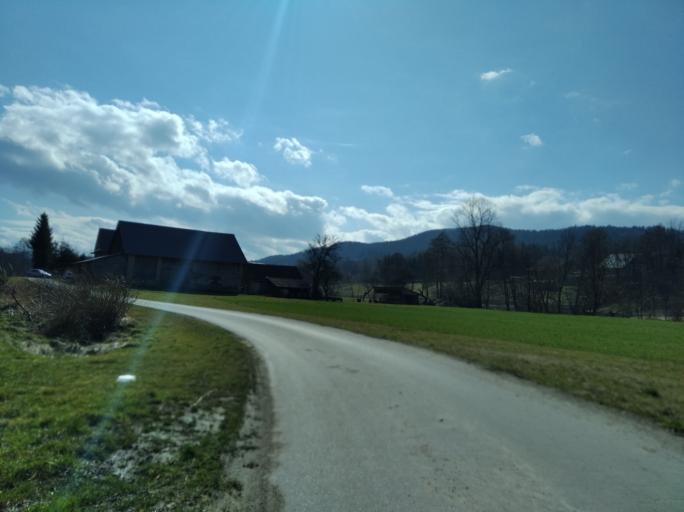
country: PL
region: Subcarpathian Voivodeship
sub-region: Powiat strzyzowski
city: Wysoka Strzyzowska
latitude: 49.8040
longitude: 21.7519
